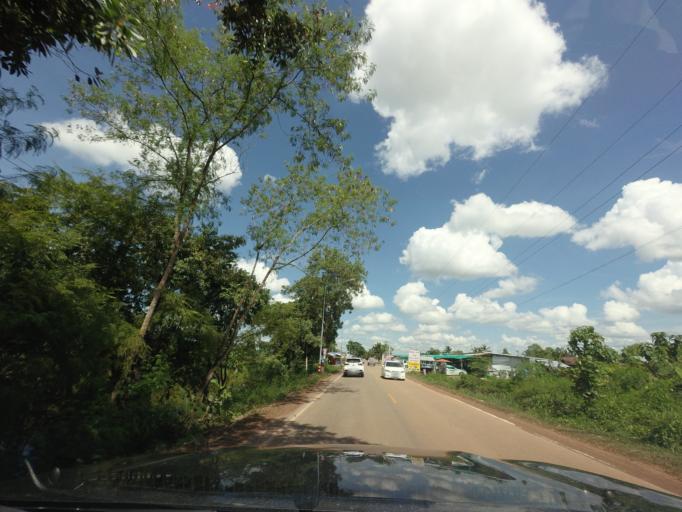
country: TH
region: Changwat Udon Thani
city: Ban Dung
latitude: 17.7402
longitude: 103.3515
